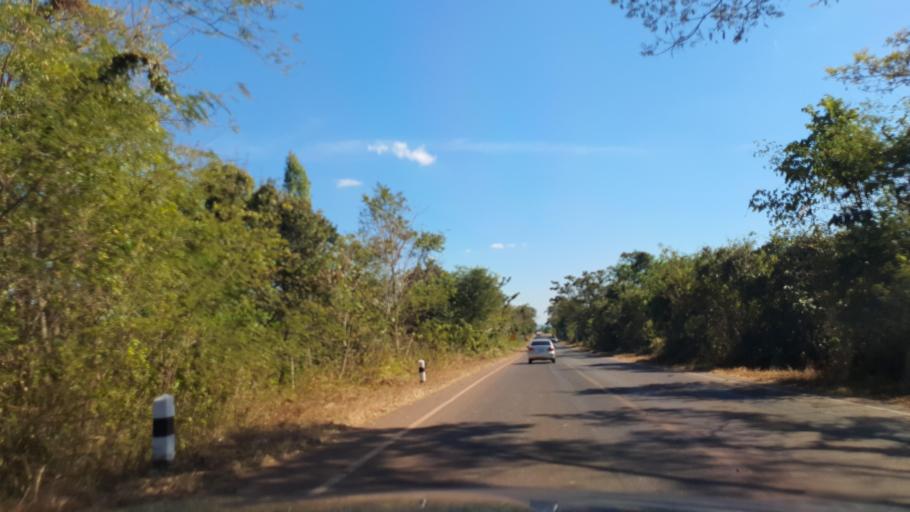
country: TH
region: Kalasin
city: Khao Wong
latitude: 16.7908
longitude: 104.1432
